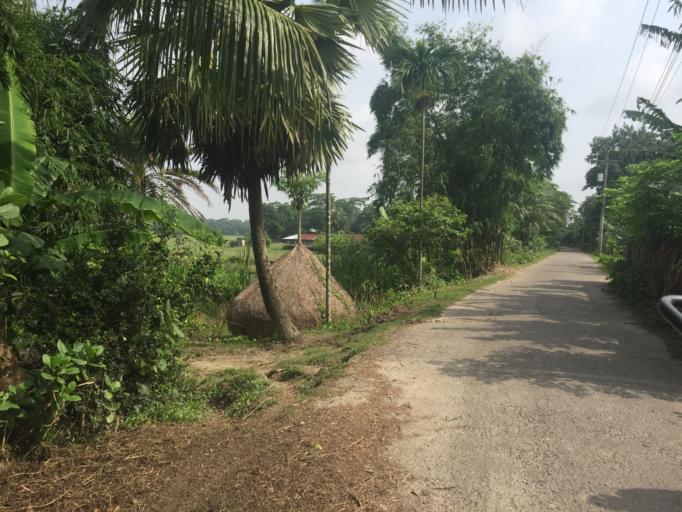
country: BD
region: Barisal
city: Mathba
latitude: 22.2273
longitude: 89.9157
